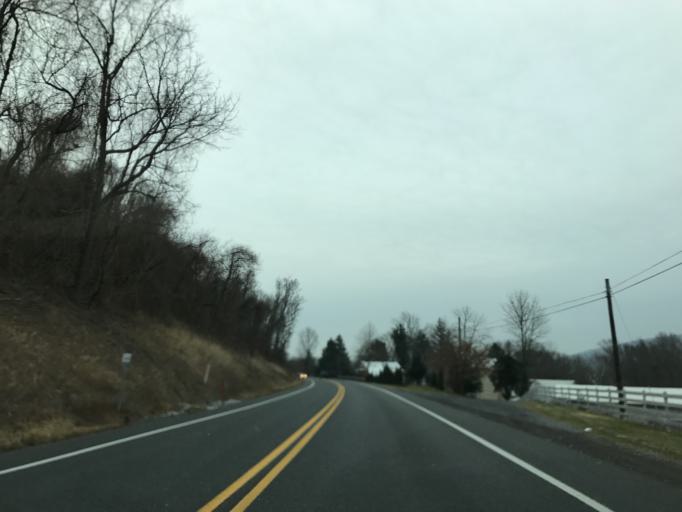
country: US
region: Pennsylvania
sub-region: Adams County
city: Carroll Valley
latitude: 39.7277
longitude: -77.3638
